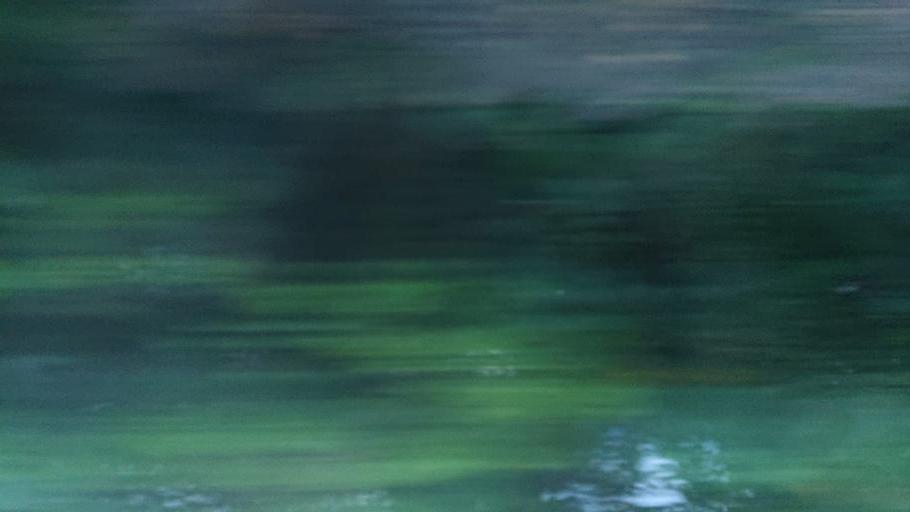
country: TW
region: Taiwan
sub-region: Taitung
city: Taitung
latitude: 23.0485
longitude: 121.1654
